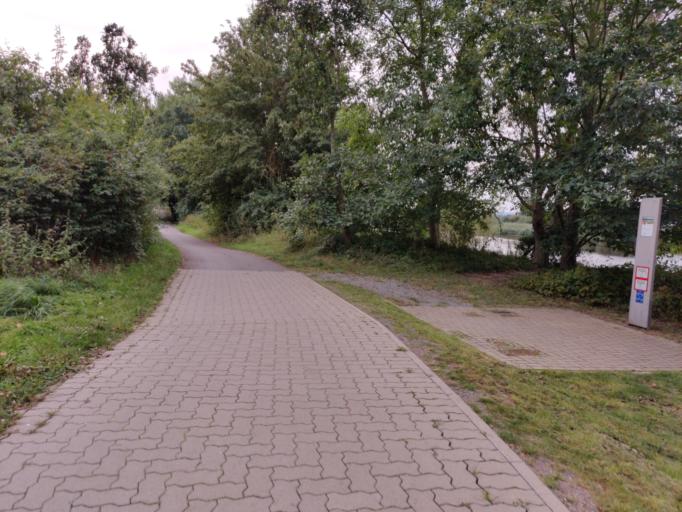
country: DE
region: Lower Saxony
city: Hameln
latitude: 52.0898
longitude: 9.3628
